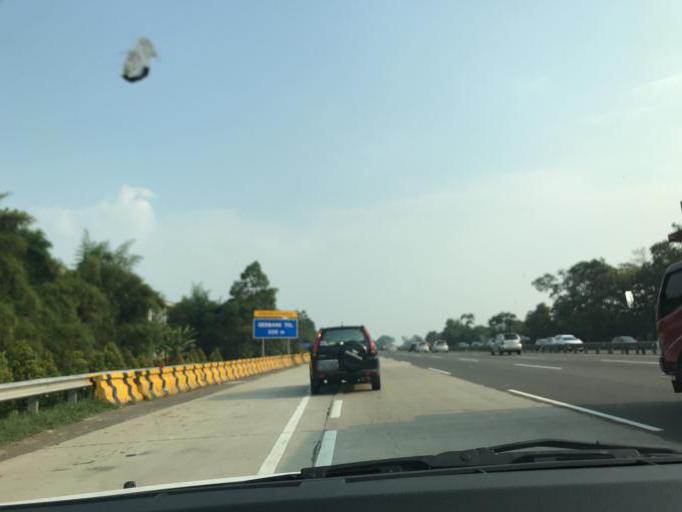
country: ID
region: West Java
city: Cibinong
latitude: -6.5276
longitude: 106.8543
